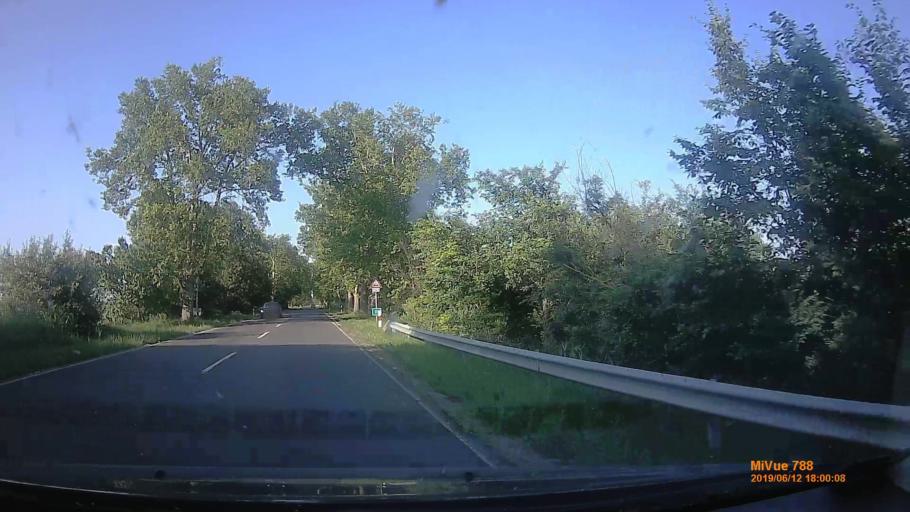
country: HU
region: Csongrad
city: Roszke
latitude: 46.2139
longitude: 20.0574
